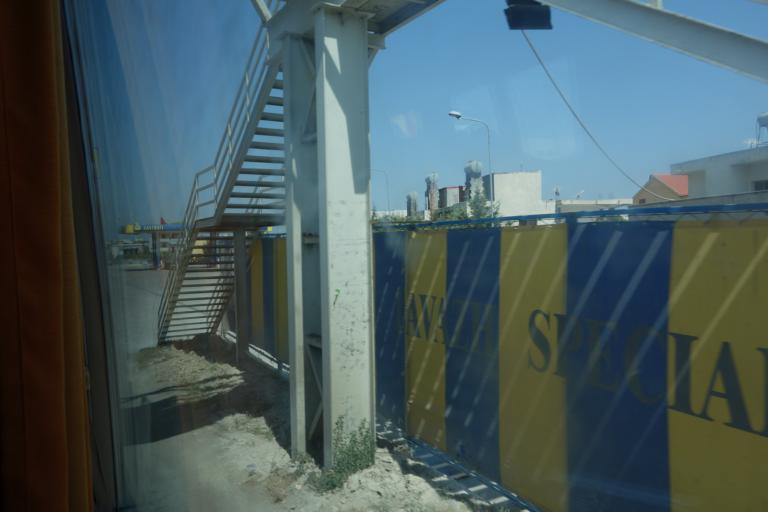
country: AL
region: Durres
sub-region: Rrethi i Durresit
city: Rrashbull
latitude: 41.3337
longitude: 19.4800
